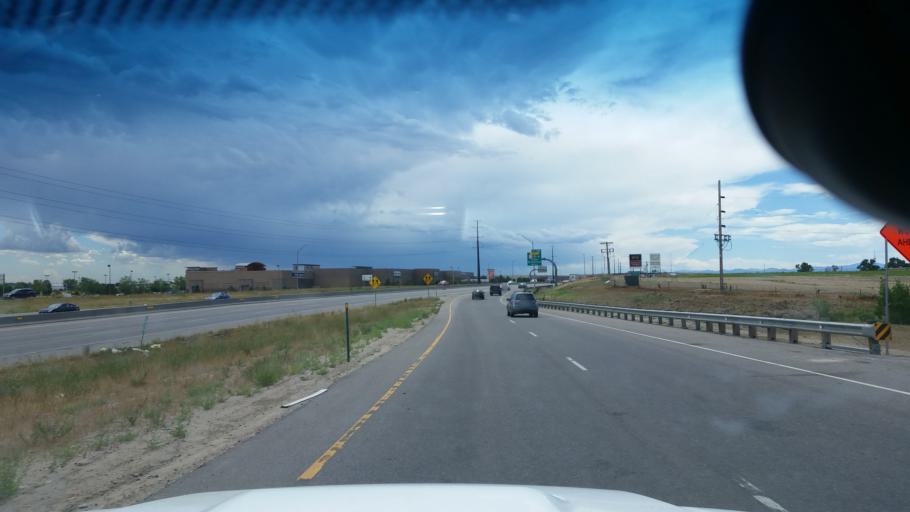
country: US
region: Colorado
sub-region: Boulder County
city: Erie
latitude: 39.9995
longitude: -104.9819
